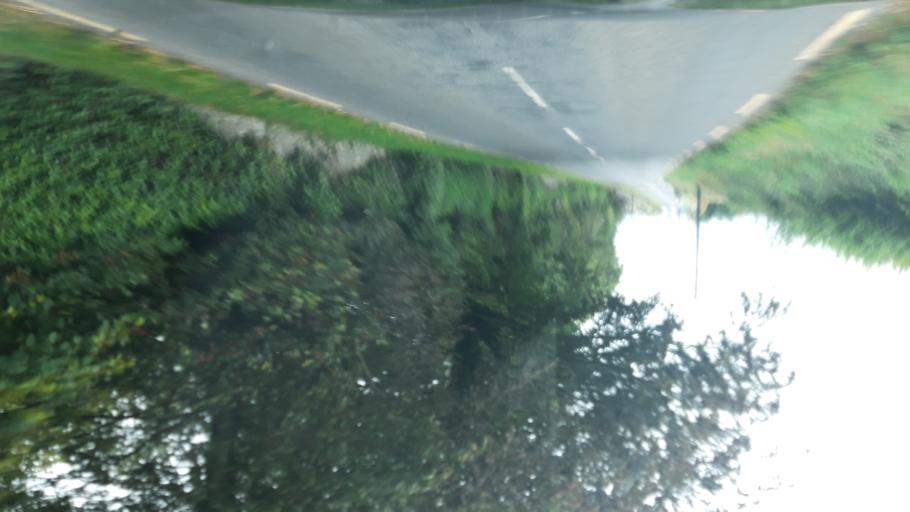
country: IE
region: Leinster
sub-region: Kilkenny
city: Ballyragget
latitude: 52.7914
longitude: -7.3269
